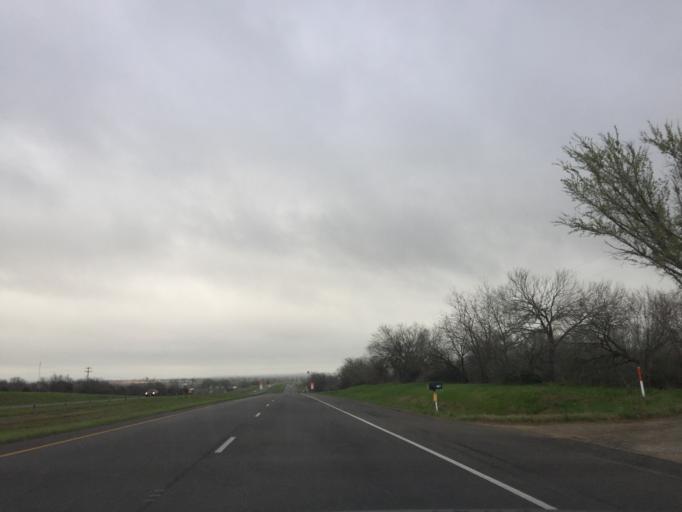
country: US
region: Texas
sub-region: Travis County
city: Garfield
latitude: 30.1867
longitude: -97.5572
